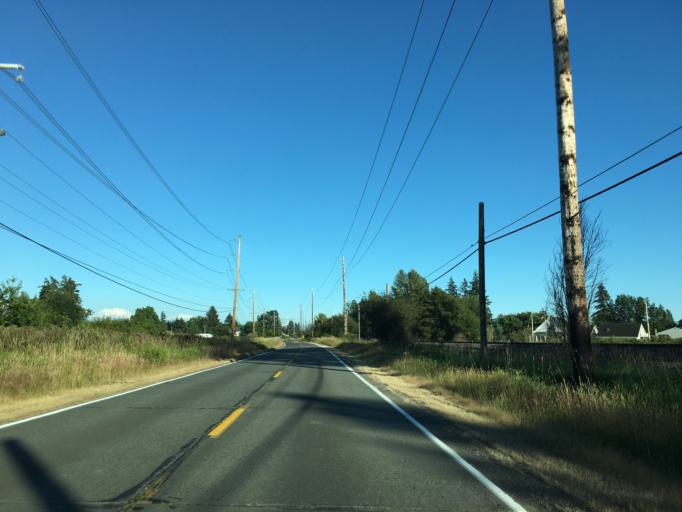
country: US
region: Washington
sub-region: Whatcom County
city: Ferndale
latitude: 48.9217
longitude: -122.6471
